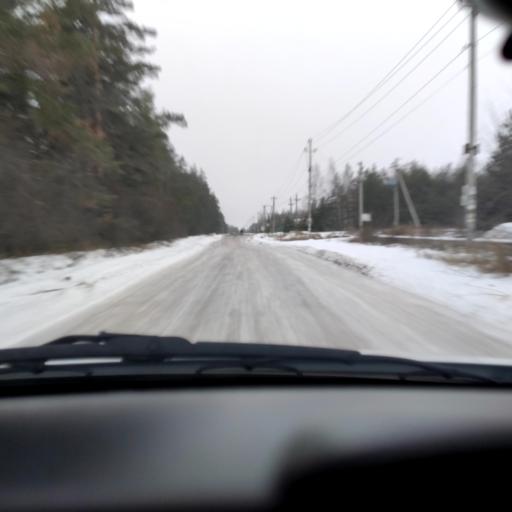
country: RU
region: Voronezj
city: Ramon'
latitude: 51.8879
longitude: 39.2515
